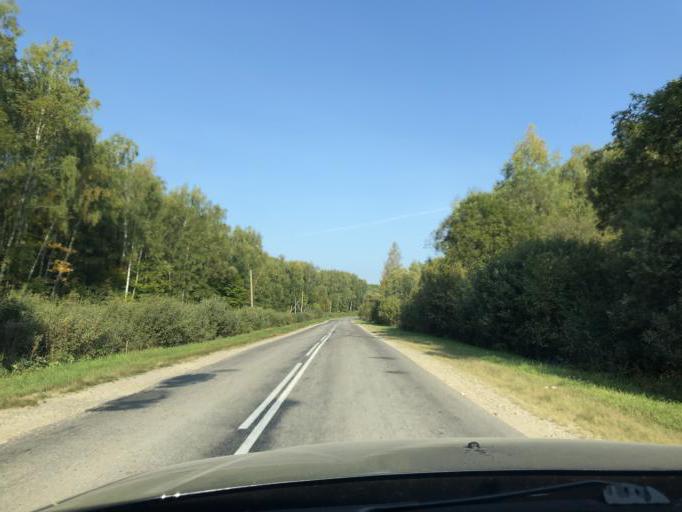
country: RU
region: Tula
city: Leninskiy
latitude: 54.3227
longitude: 37.4001
